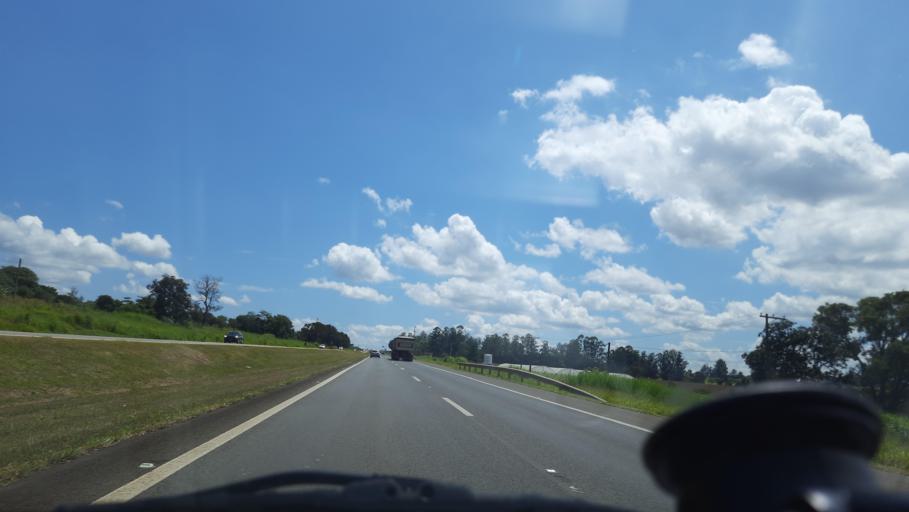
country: BR
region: Sao Paulo
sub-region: Moji-Guacu
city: Mogi-Gaucu
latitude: -22.2363
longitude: -46.9783
